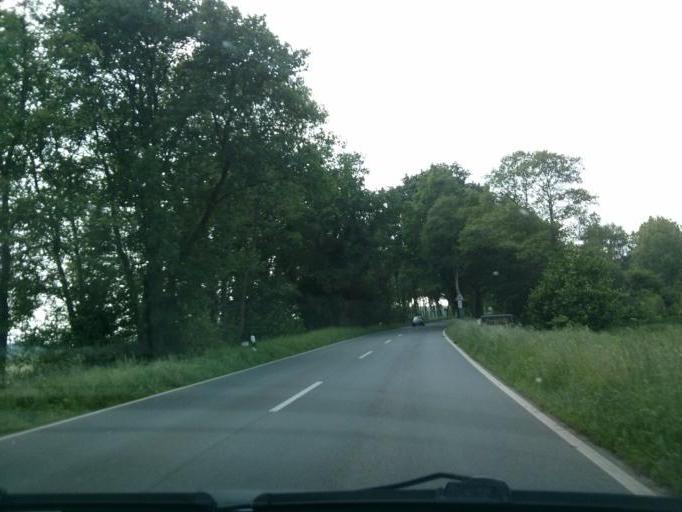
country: DE
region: Lower Saxony
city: Schiffdorf
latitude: 53.5146
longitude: 8.6954
